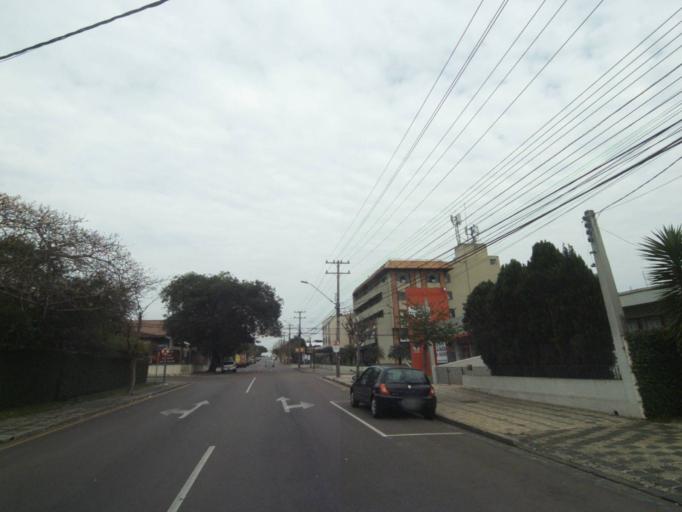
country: BR
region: Parana
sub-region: Curitiba
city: Curitiba
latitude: -25.4561
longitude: -49.3072
